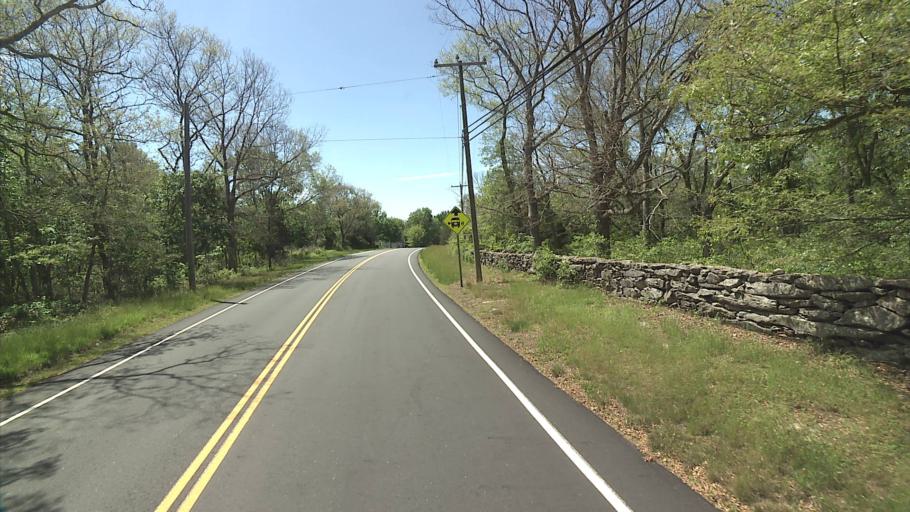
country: US
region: Connecticut
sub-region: Windham County
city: Moosup
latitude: 41.6847
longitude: -71.8491
